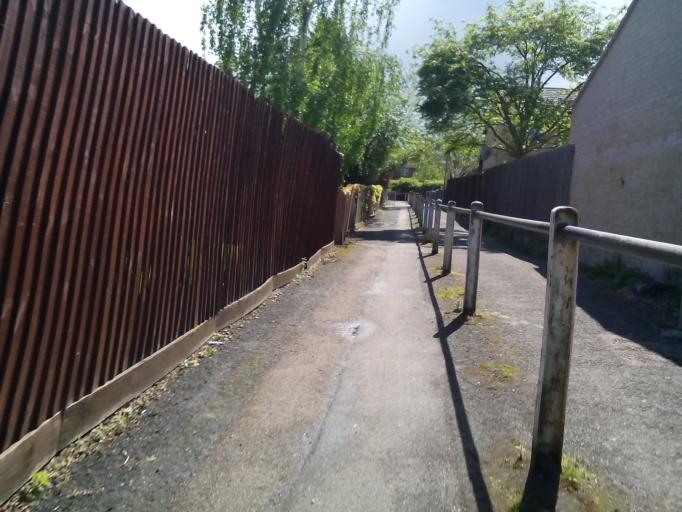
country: GB
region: England
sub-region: Cambridgeshire
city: Cambridge
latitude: 52.1849
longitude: 0.1630
